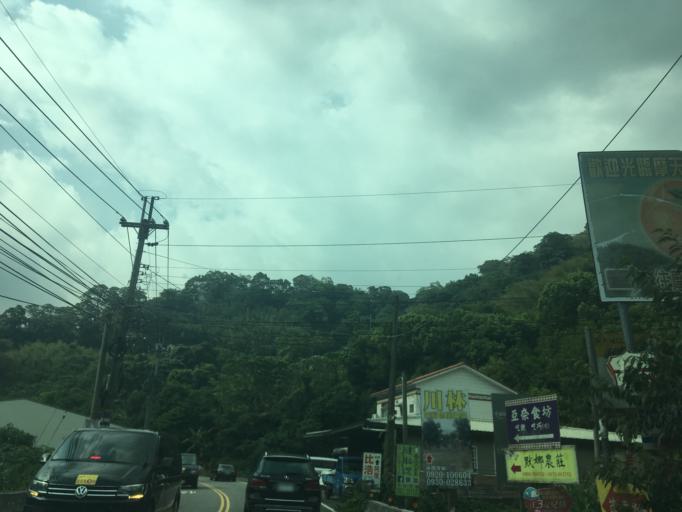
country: TW
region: Taiwan
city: Fengyuan
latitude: 24.3188
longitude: 120.9240
